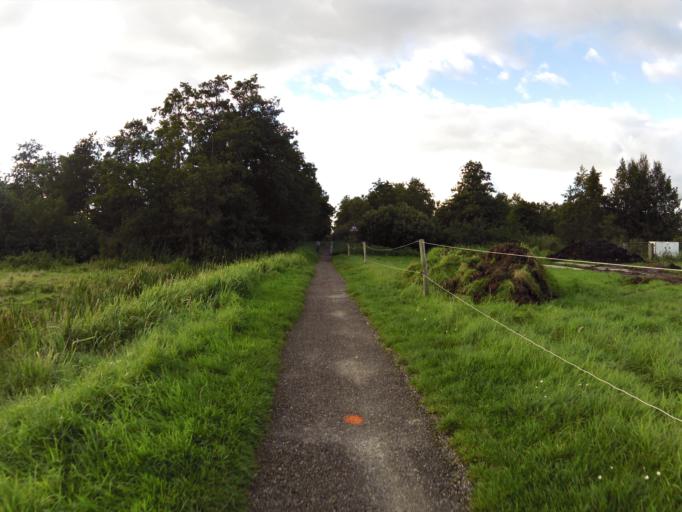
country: NL
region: South Holland
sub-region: Gemeente Nieuwkoop
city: Nieuwkoop
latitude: 52.1238
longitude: 4.7832
